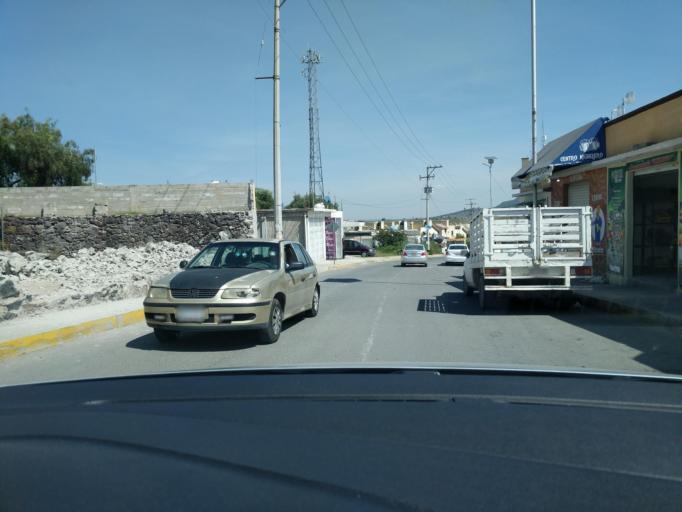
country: MX
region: Hidalgo
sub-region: Atotonilco de Tula
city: Paseos de la Pradera
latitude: 19.9325
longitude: -99.2346
